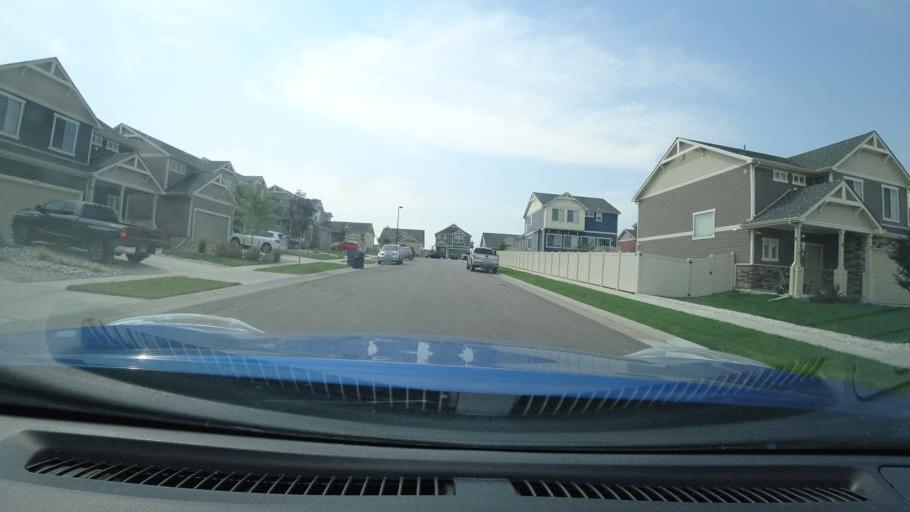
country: US
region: Colorado
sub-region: Adams County
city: Aurora
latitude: 39.7775
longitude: -104.7776
